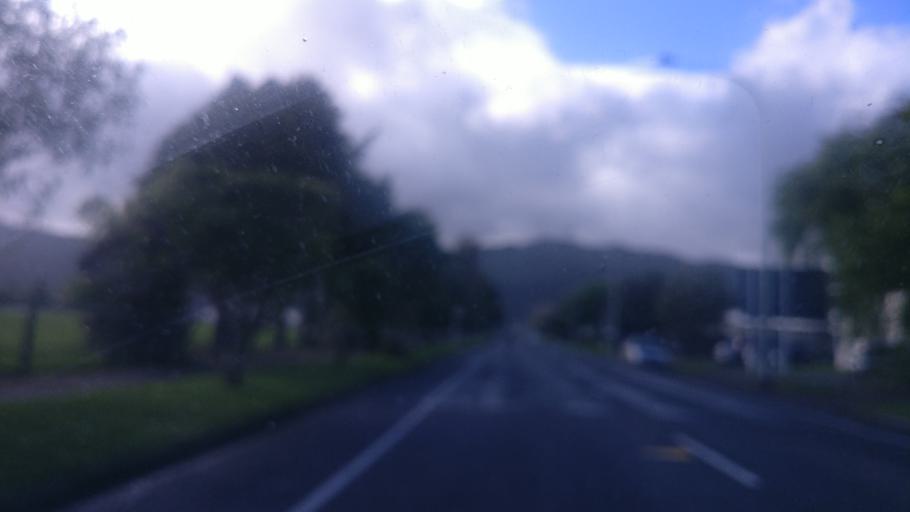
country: NZ
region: Wellington
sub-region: Lower Hutt City
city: Lower Hutt
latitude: -41.1978
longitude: 174.9384
